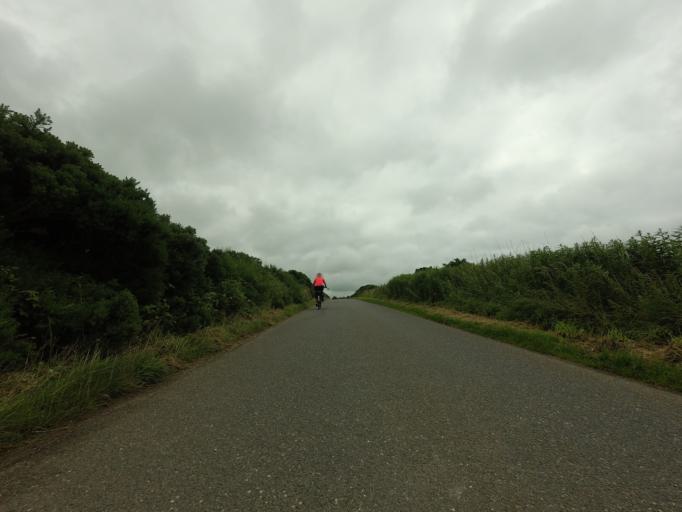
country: GB
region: Scotland
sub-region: Aberdeenshire
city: Turriff
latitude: 57.5437
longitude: -2.2774
